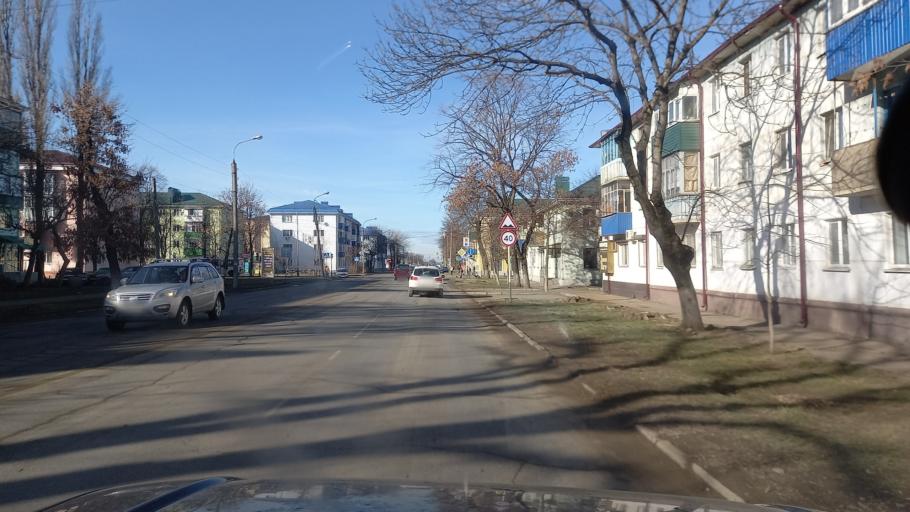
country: RU
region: Adygeya
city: Maykop
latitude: 44.6174
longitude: 40.1082
